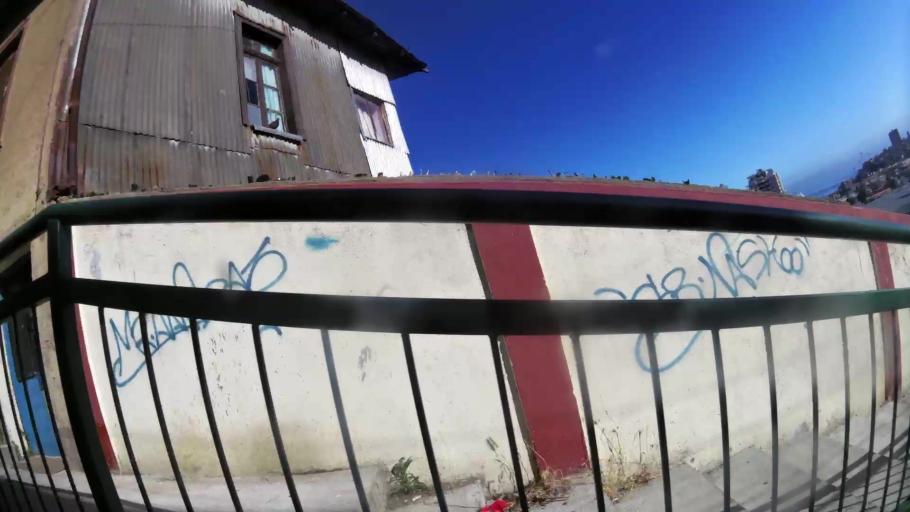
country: CL
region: Valparaiso
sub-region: Provincia de Valparaiso
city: Valparaiso
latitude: -33.0535
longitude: -71.6098
